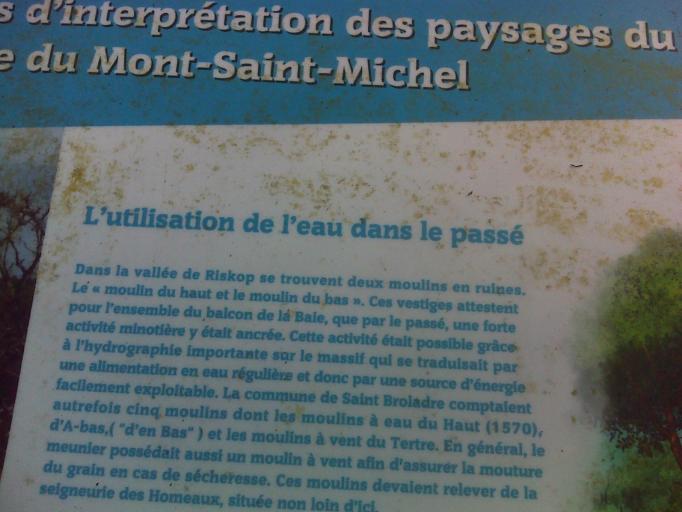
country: FR
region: Brittany
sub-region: Departement d'Ille-et-Vilaine
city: Saint-Broladre
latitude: 48.5827
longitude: -1.6549
